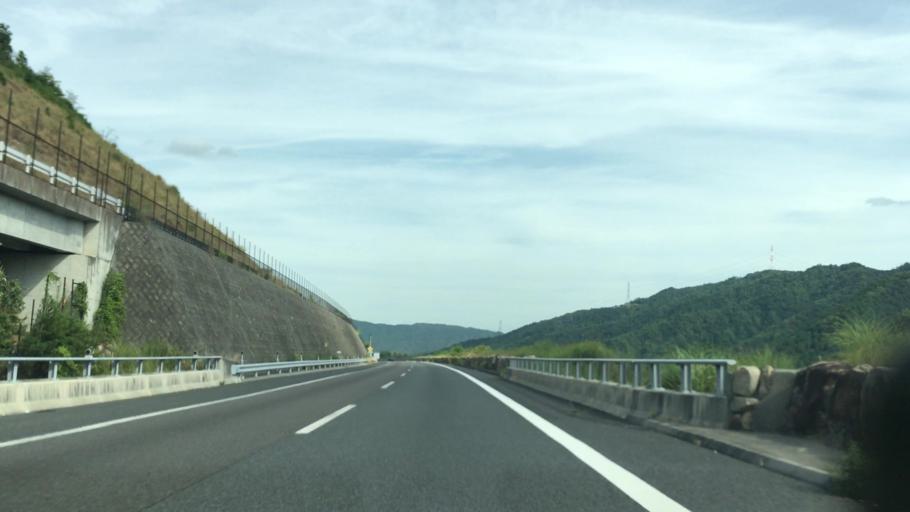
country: JP
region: Shiga Prefecture
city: Kusatsu
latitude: 34.9353
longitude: 136.0410
